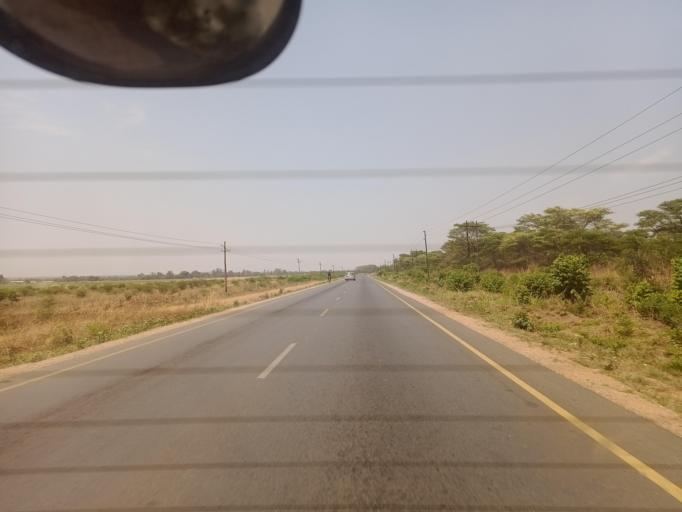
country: ZM
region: Lusaka
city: Lusaka
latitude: -15.2687
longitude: 28.4165
